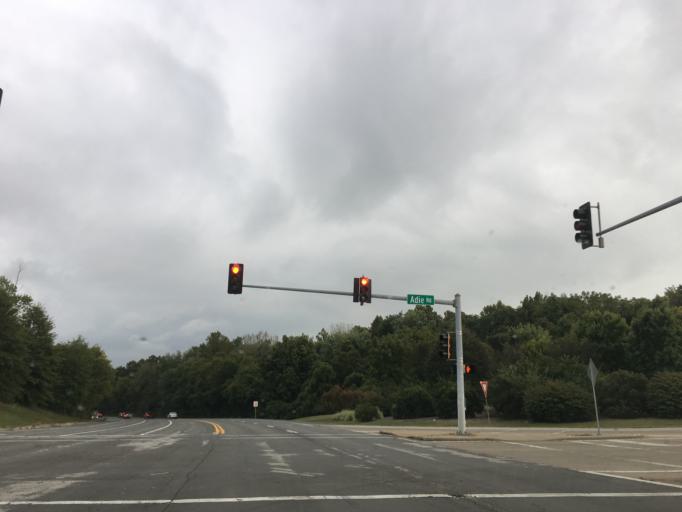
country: US
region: Missouri
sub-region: Saint Louis County
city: Maryland Heights
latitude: 38.7088
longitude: -90.4148
